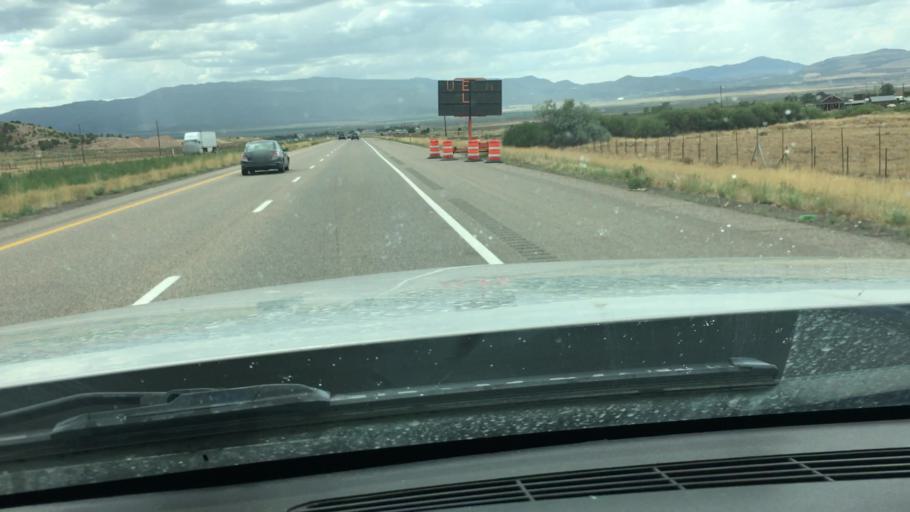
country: US
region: Utah
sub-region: Iron County
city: Cedar City
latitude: 37.6272
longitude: -113.1261
